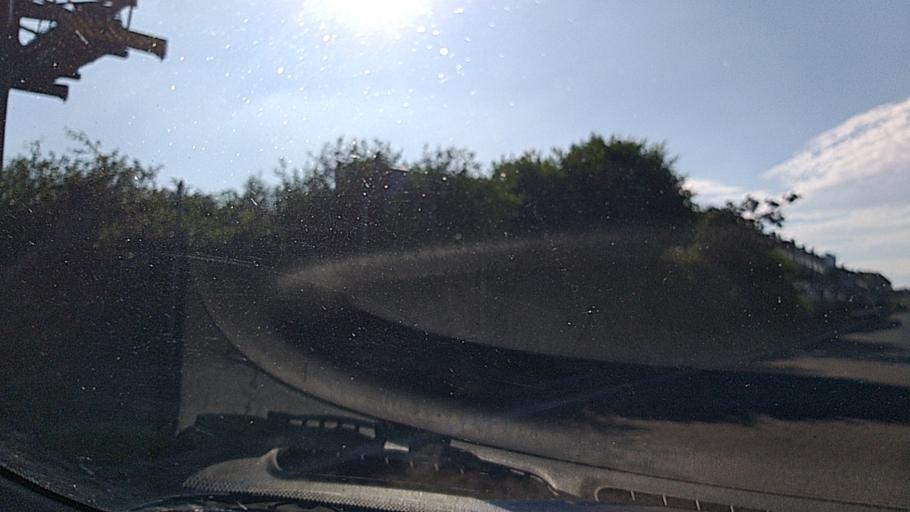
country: AU
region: New South Wales
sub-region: Wollongong
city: Port Kembla
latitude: -34.4794
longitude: 150.9072
